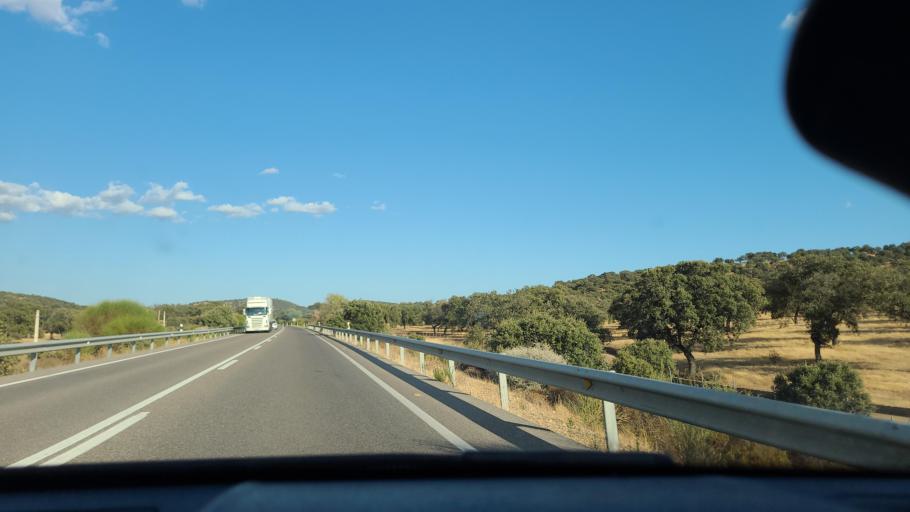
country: ES
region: Andalusia
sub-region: Province of Cordoba
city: Belmez
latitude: 38.2066
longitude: -5.1256
